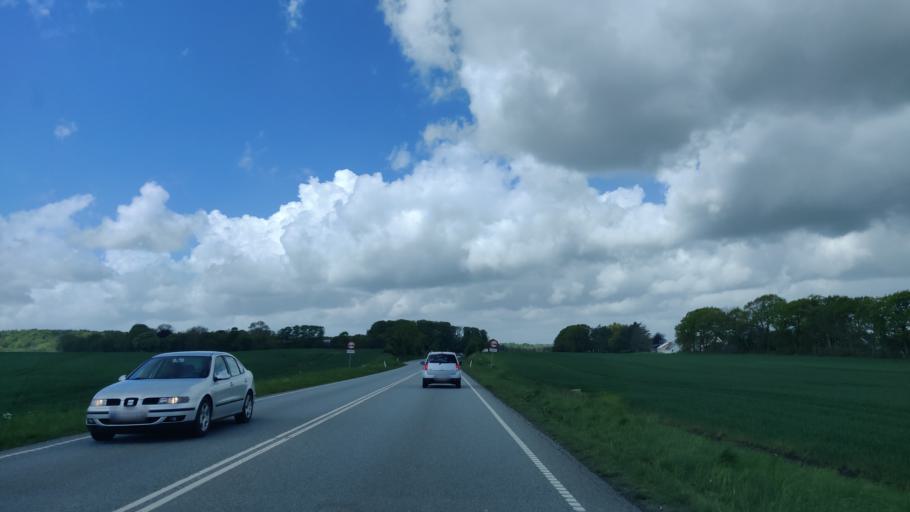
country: DK
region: Central Jutland
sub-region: Hedensted Kommune
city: Torring
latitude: 55.8458
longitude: 9.4841
